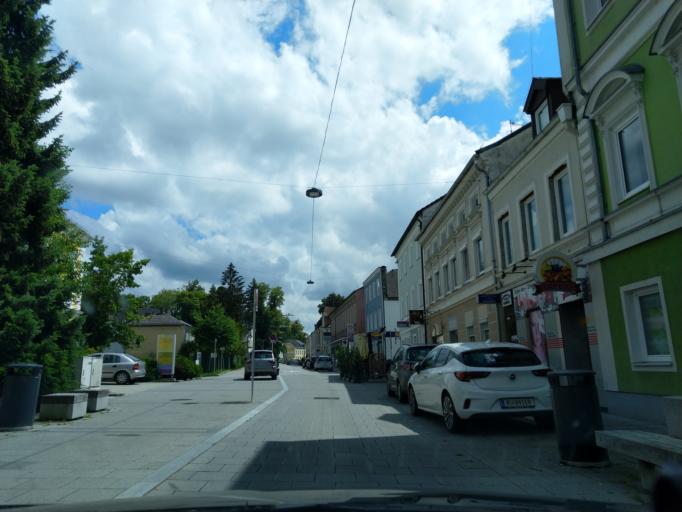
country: AT
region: Upper Austria
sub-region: Politischer Bezirk Ried im Innkreis
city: Ried im Innkreis
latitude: 48.2069
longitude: 13.4879
